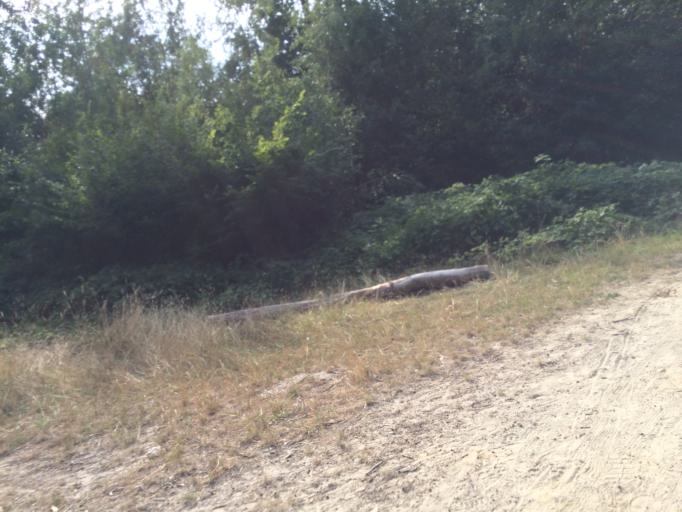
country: FR
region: Ile-de-France
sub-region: Departement de l'Essonne
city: Epinay-sous-Senart
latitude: 48.6819
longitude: 2.5080
